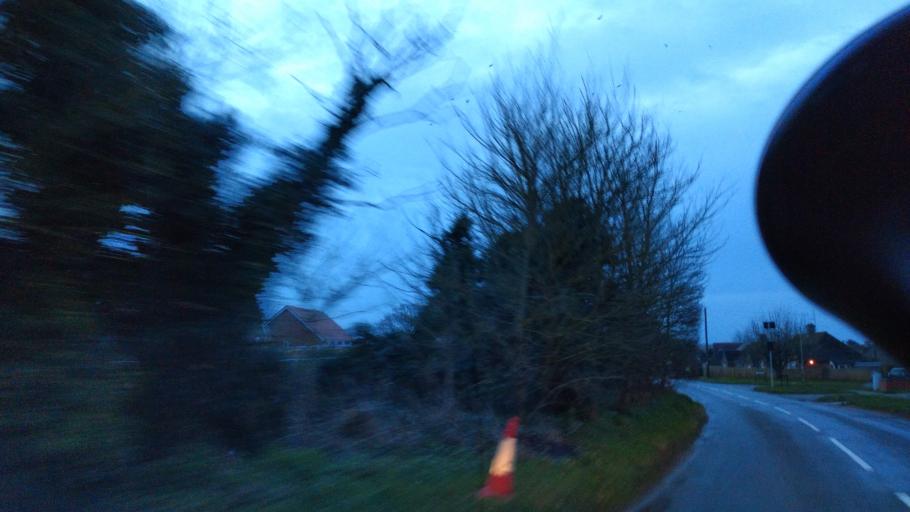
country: GB
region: England
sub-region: Oxfordshire
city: Shrivenham
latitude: 51.6014
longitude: -1.6626
